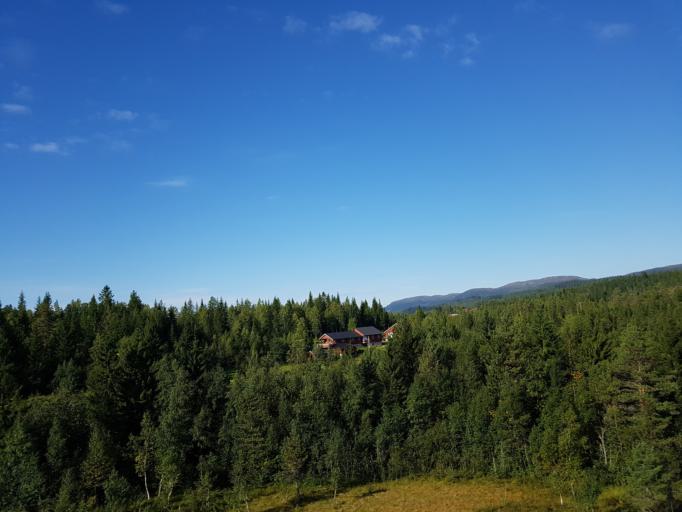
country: NO
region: Sor-Trondelag
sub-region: Trondheim
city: Trondheim
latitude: 63.6430
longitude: 10.2696
